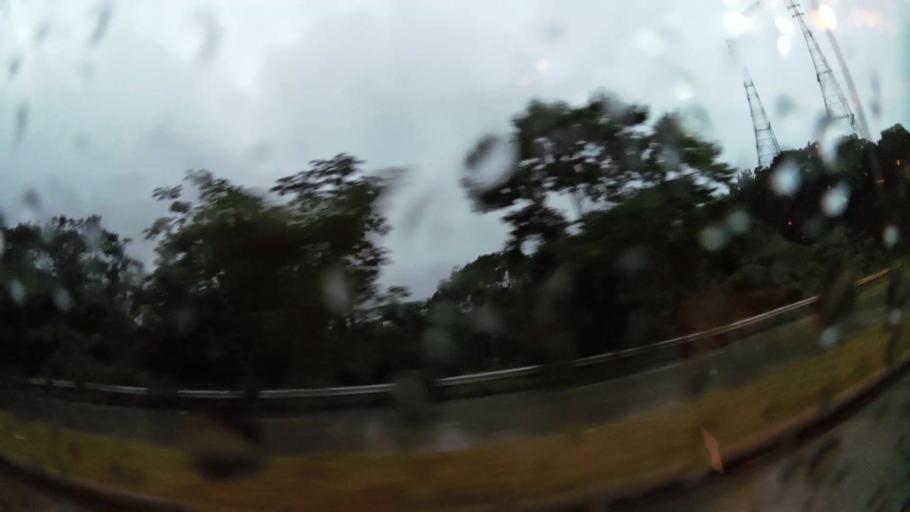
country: PA
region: Panama
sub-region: Distrito de Panama
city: Paraiso
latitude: 9.0353
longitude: -79.6288
